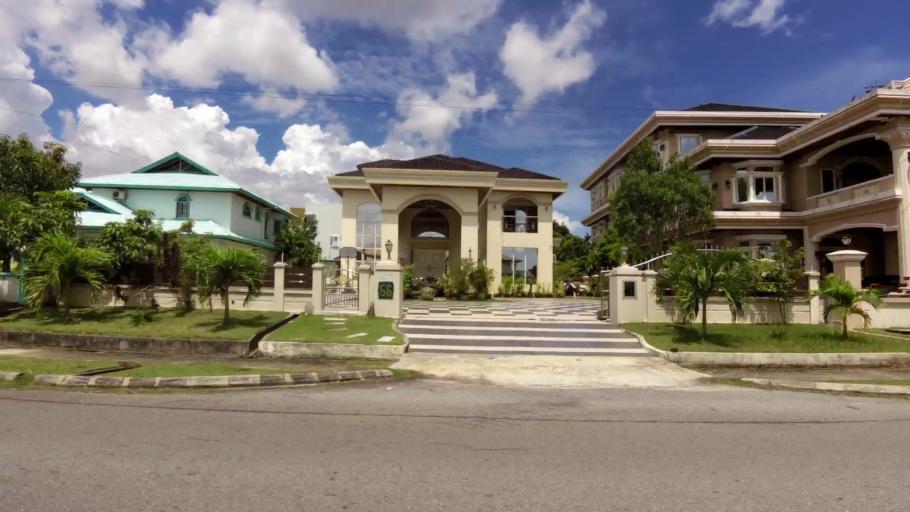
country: BN
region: Brunei and Muara
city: Bandar Seri Begawan
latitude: 4.9480
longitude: 114.9085
